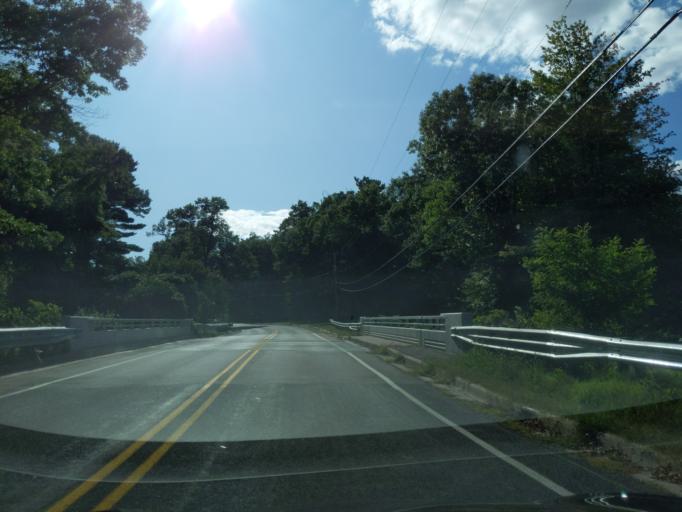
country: US
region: Michigan
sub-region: Muskegon County
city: North Muskegon
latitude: 43.2495
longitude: -86.3120
